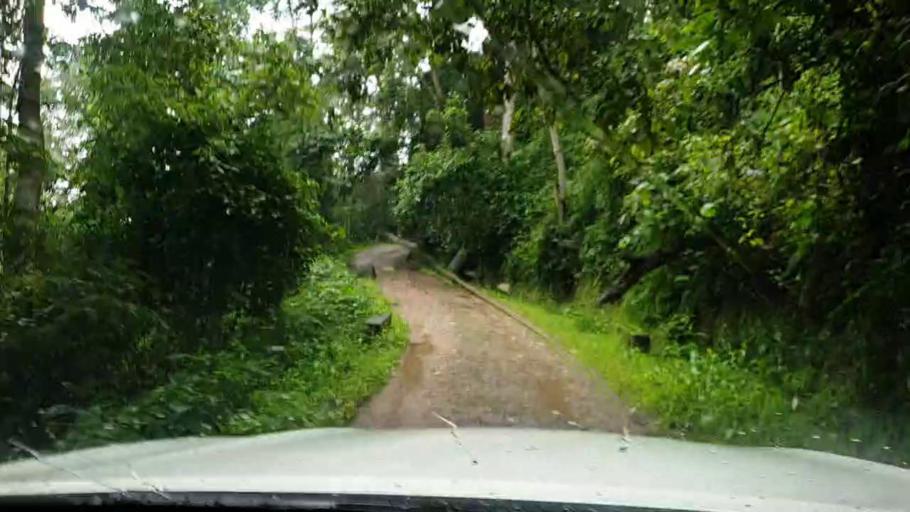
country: RW
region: Western Province
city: Cyangugu
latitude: -2.5587
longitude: 28.9869
